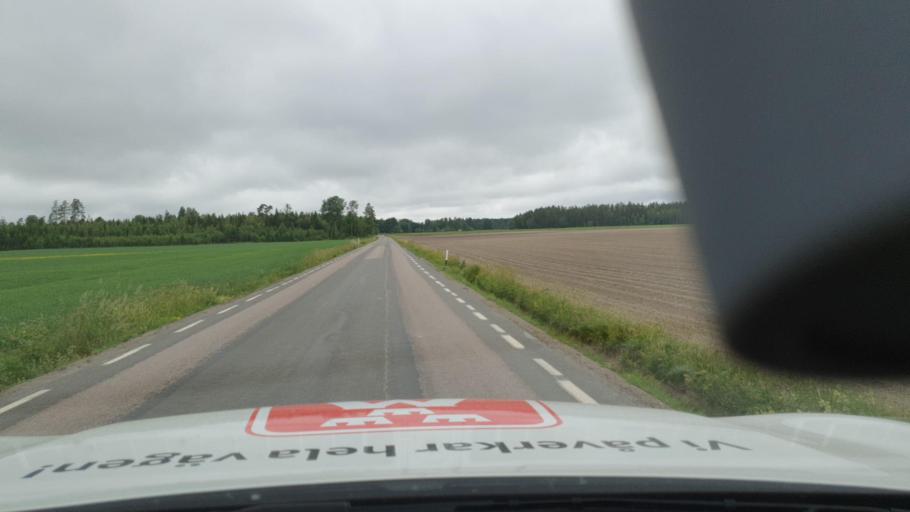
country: SE
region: Vaestra Goetaland
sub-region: Tibro Kommun
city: Tibro
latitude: 58.3976
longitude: 14.0657
